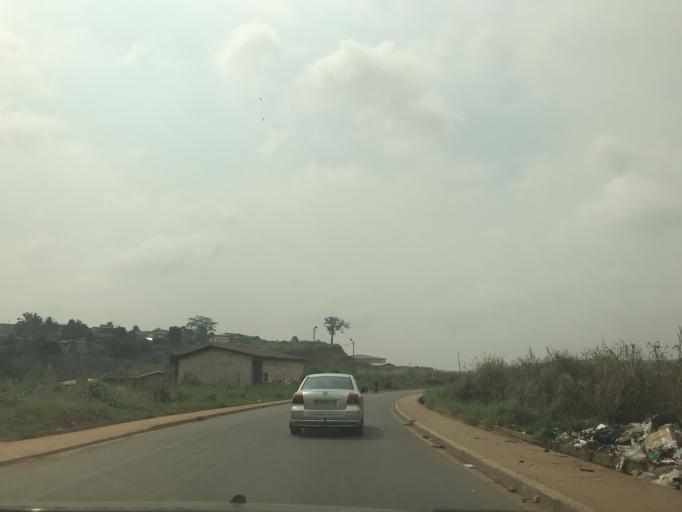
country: CM
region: Centre
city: Yaounde
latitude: 3.8272
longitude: 11.5134
